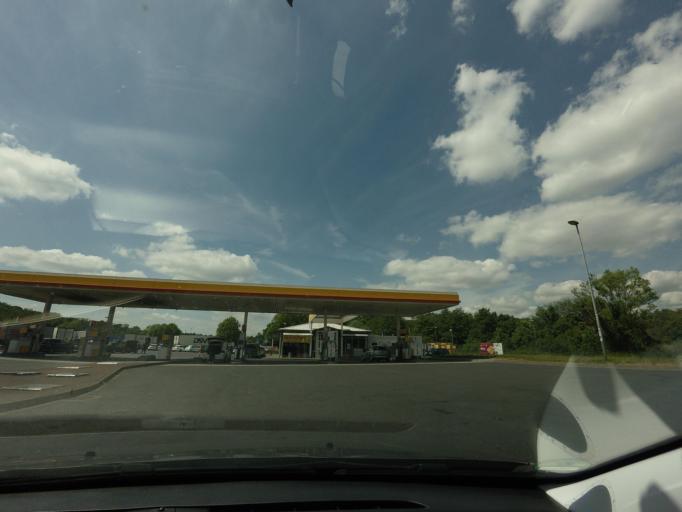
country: DE
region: Lower Saxony
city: Wendeburg
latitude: 52.3405
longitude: 10.3602
